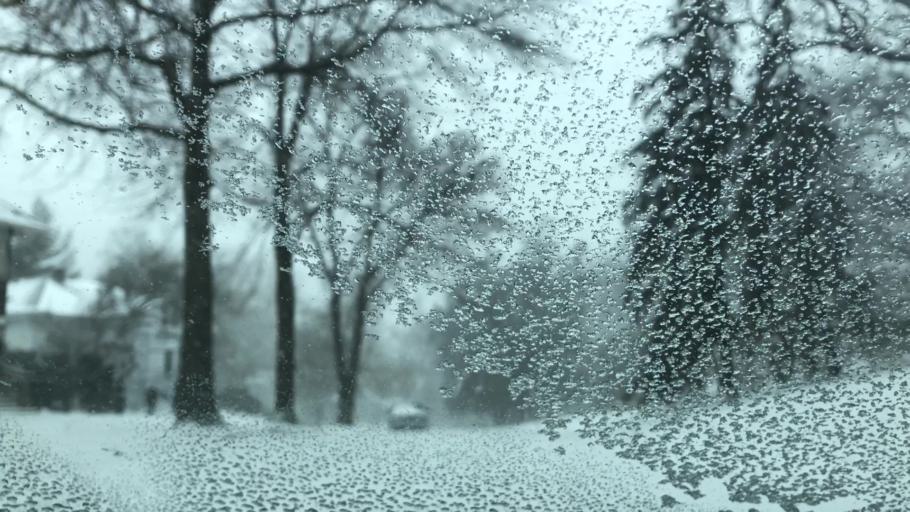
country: US
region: Iowa
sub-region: Marshall County
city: Marshalltown
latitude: 42.0543
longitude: -92.9212
